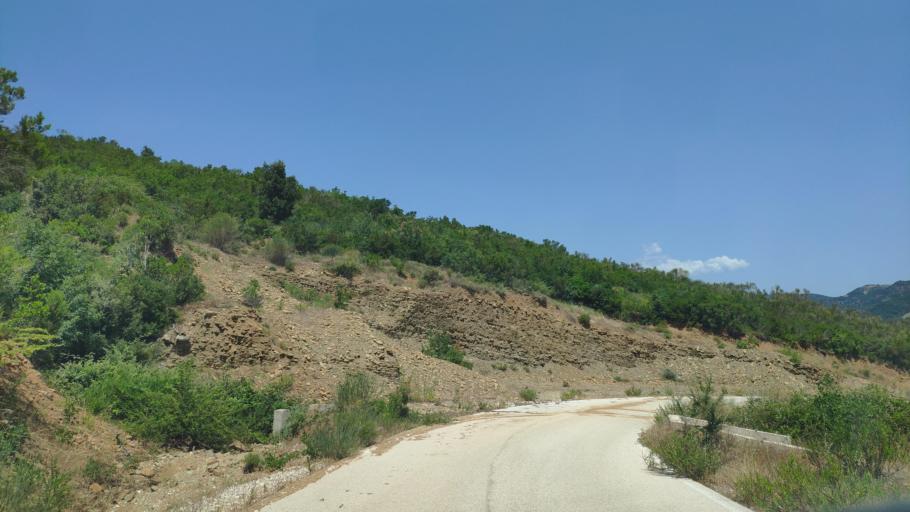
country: GR
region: West Greece
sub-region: Nomos Aitolias kai Akarnanias
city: Sardinia
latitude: 38.8835
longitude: 21.2794
